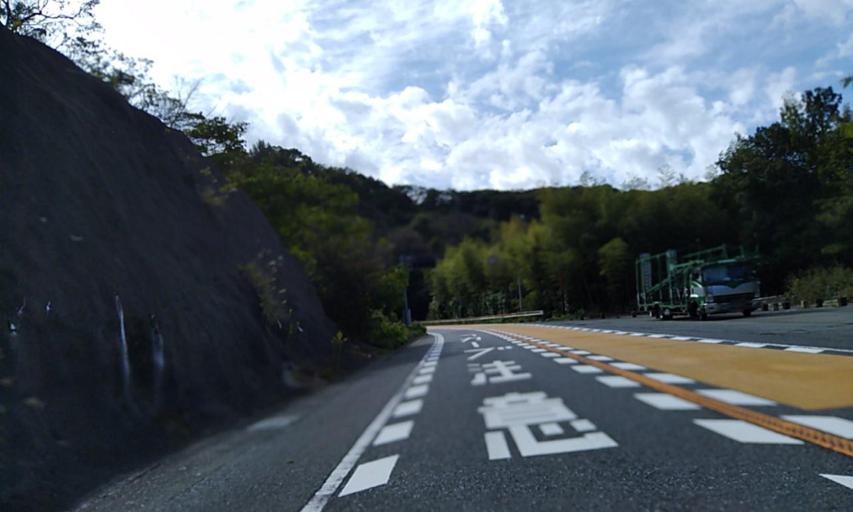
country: JP
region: Wakayama
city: Gobo
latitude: 33.9581
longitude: 135.1230
